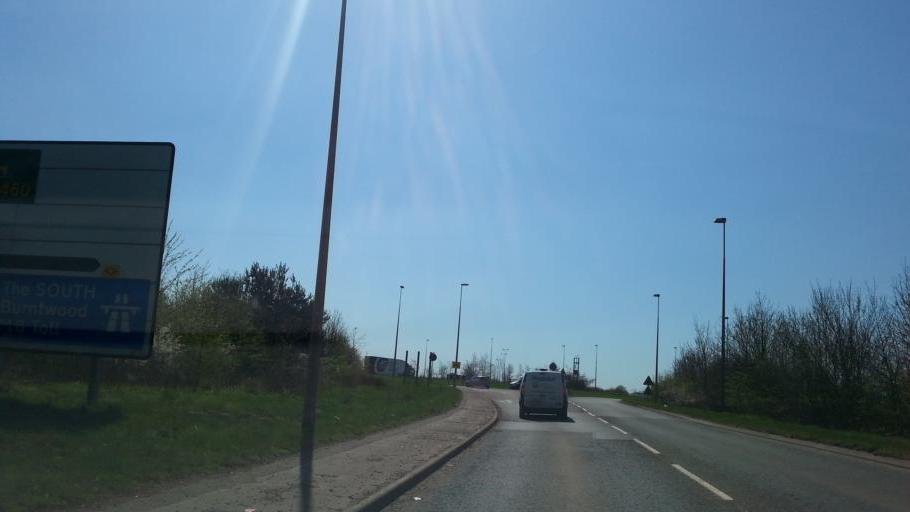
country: GB
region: England
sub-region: Staffordshire
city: Cannock
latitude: 52.6672
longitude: -2.0571
